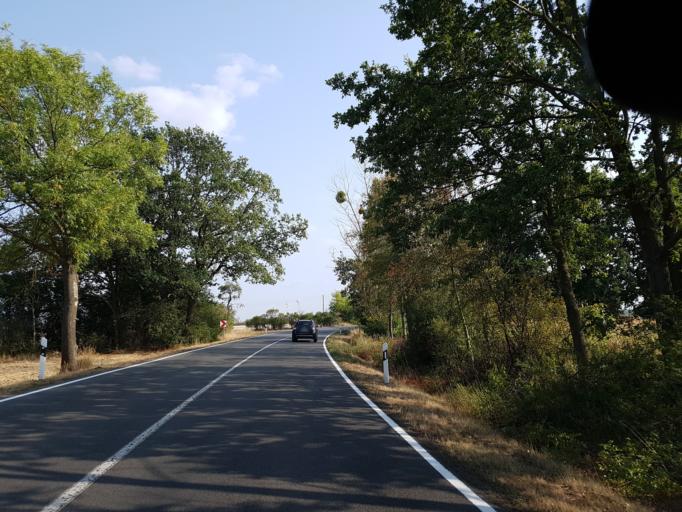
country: DE
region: Saxony-Anhalt
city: Muhlanger
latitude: 51.7944
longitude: 12.7038
